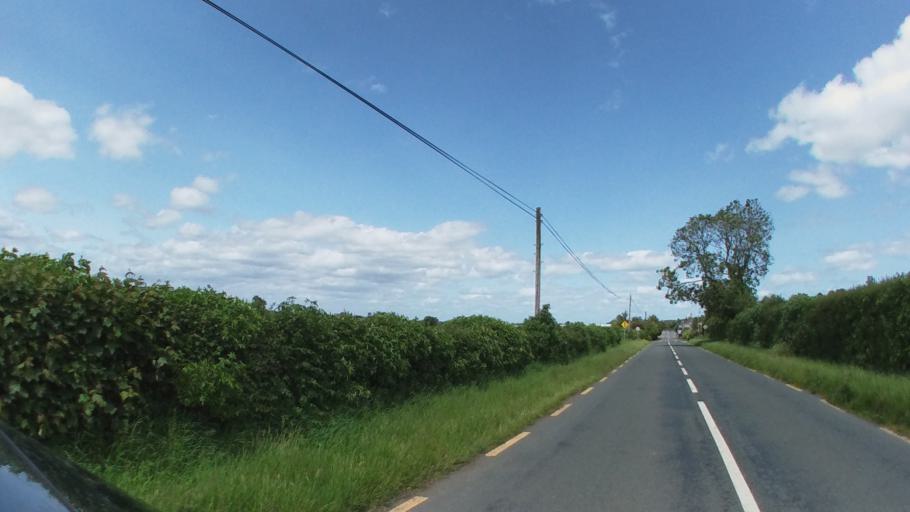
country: IE
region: Leinster
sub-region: Kildare
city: Moone
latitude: 53.0154
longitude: -6.8036
